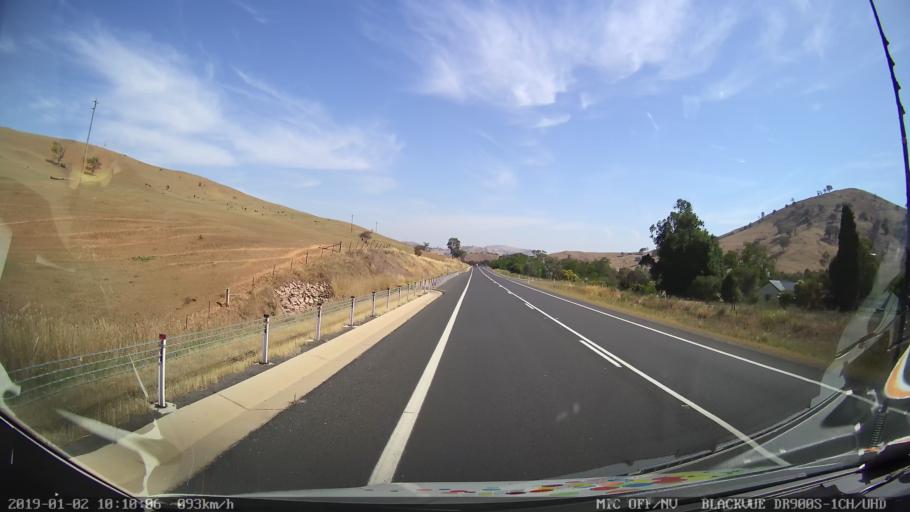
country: AU
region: New South Wales
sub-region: Gundagai
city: Gundagai
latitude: -35.1086
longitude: 148.0970
